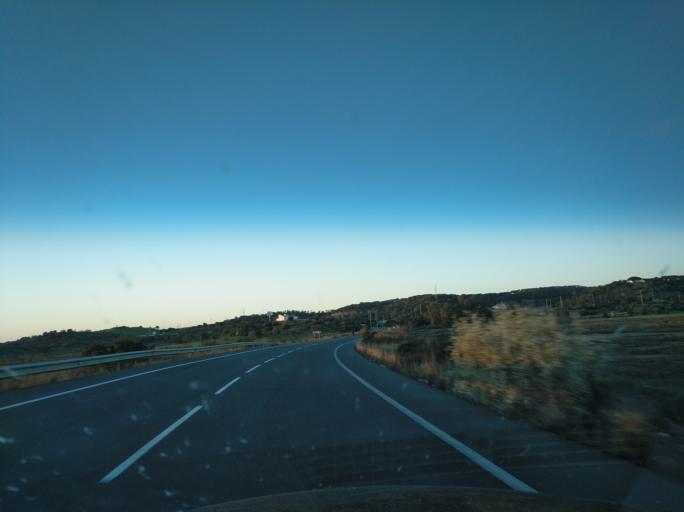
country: ES
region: Andalusia
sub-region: Provincia de Huelva
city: Ayamonte
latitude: 37.2331
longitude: -7.4037
